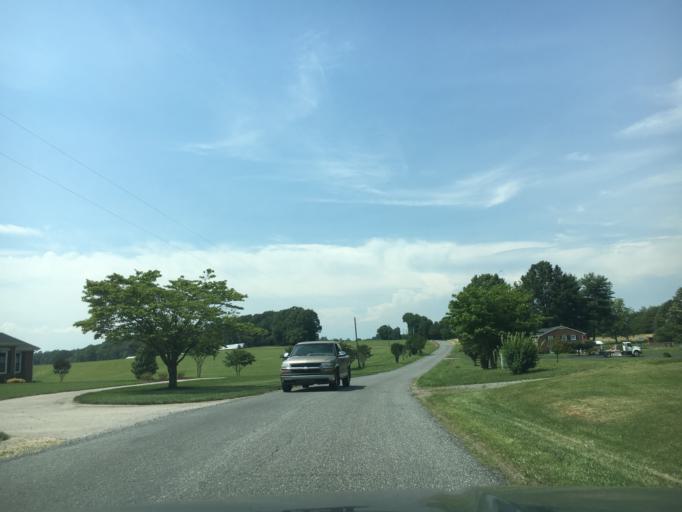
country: US
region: Virginia
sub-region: Pittsylvania County
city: Gretna
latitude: 36.9132
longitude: -79.4208
